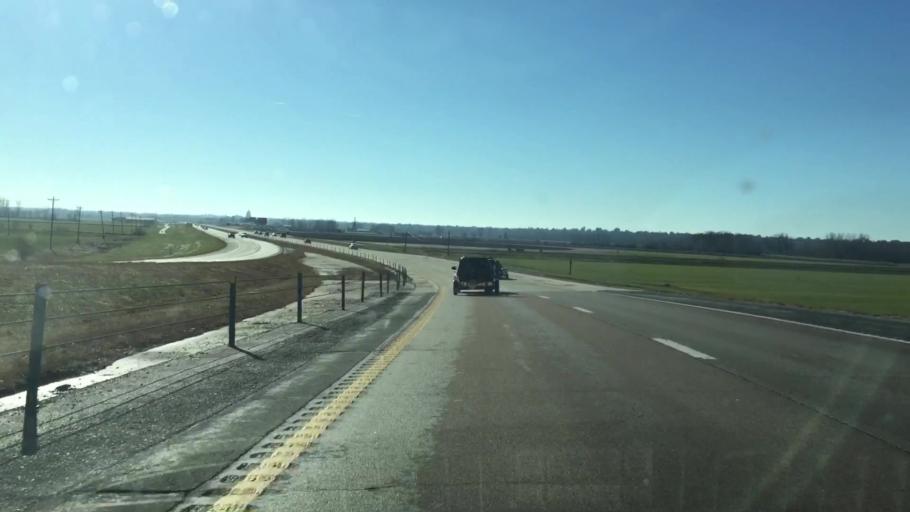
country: US
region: Missouri
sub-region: Cole County
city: Jefferson City
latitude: 38.6324
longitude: -92.1971
